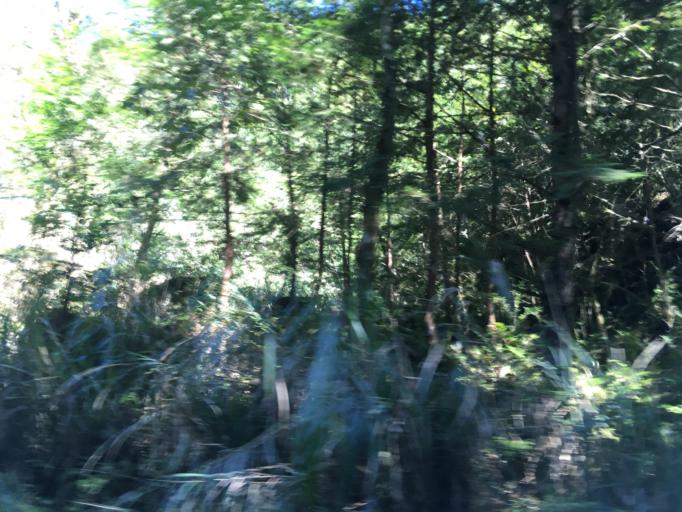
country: TW
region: Taiwan
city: Daxi
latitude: 24.5903
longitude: 121.4125
